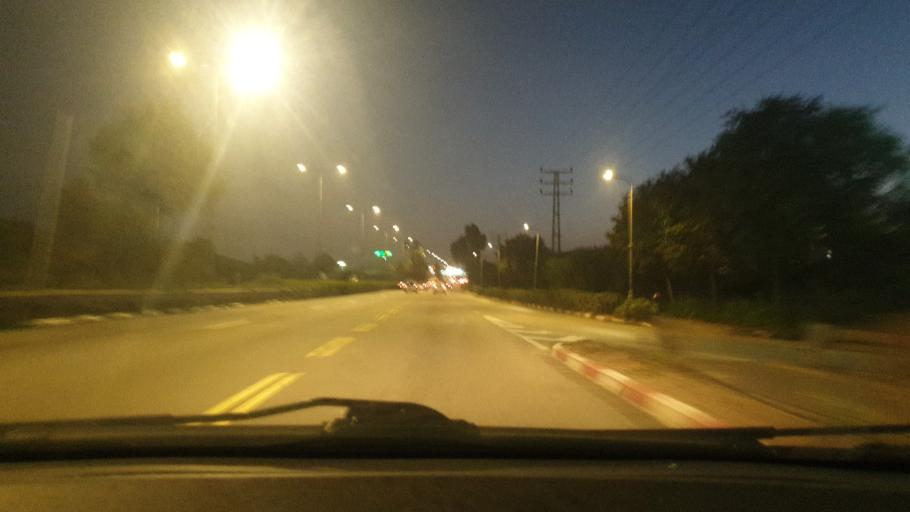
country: IL
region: Central District
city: Bet Dagan
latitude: 31.9897
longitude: 34.8121
